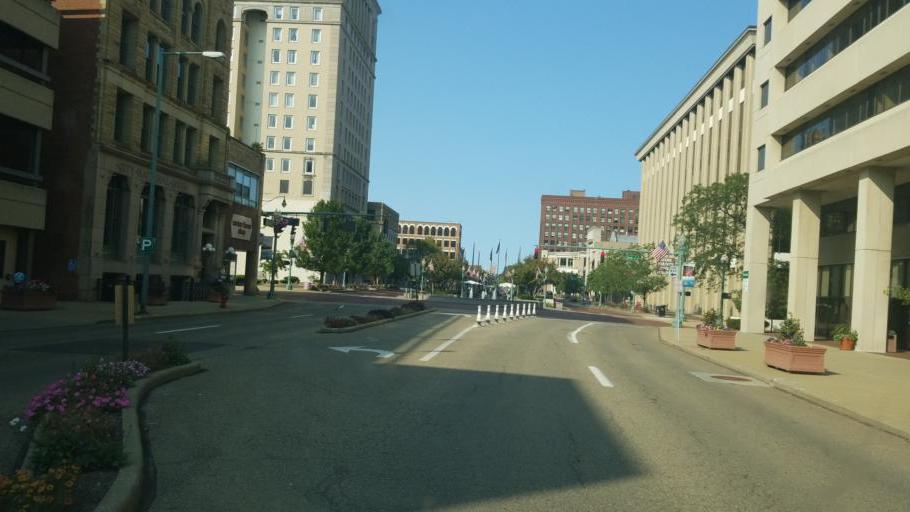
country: US
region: Ohio
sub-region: Stark County
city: Canton
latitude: 40.7972
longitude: -81.3751
